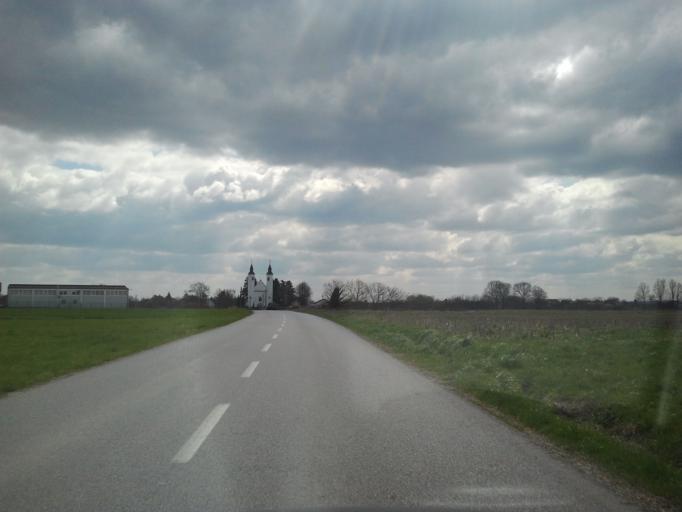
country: HR
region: Grad Zagreb
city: Brezovica
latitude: 45.7350
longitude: 15.8924
